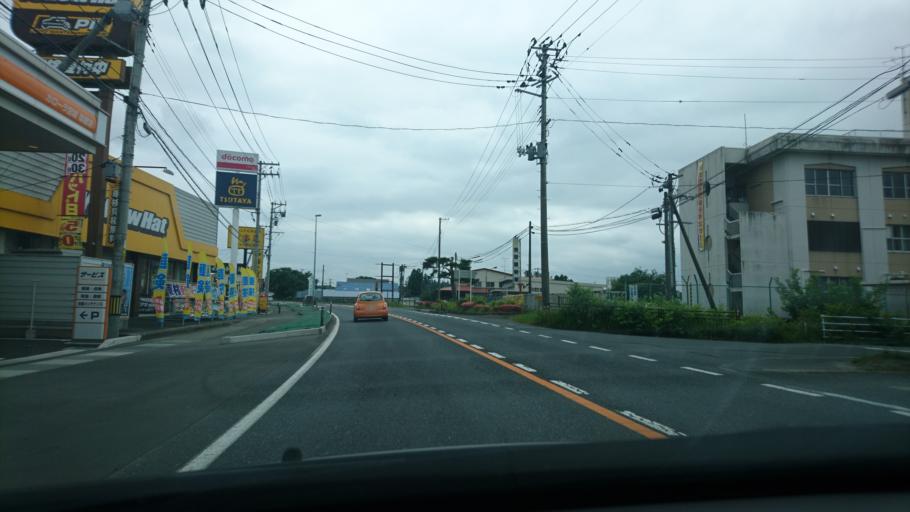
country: JP
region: Miyagi
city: Furukawa
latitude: 38.7445
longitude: 141.0153
